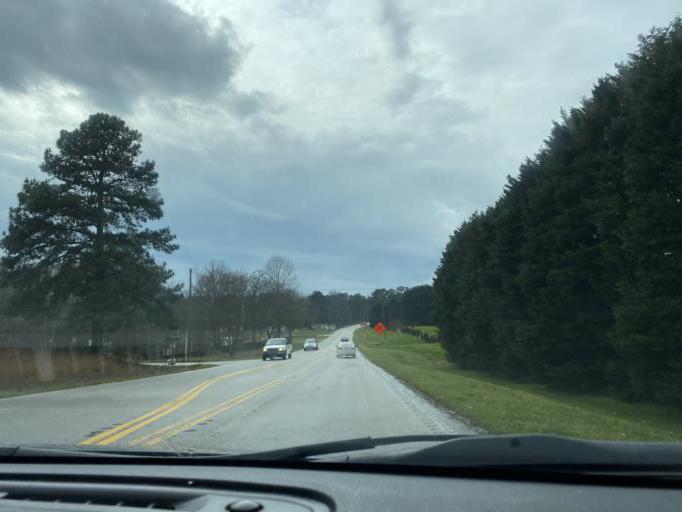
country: US
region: South Carolina
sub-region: Spartanburg County
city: Cowpens
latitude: 35.0181
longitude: -81.7791
